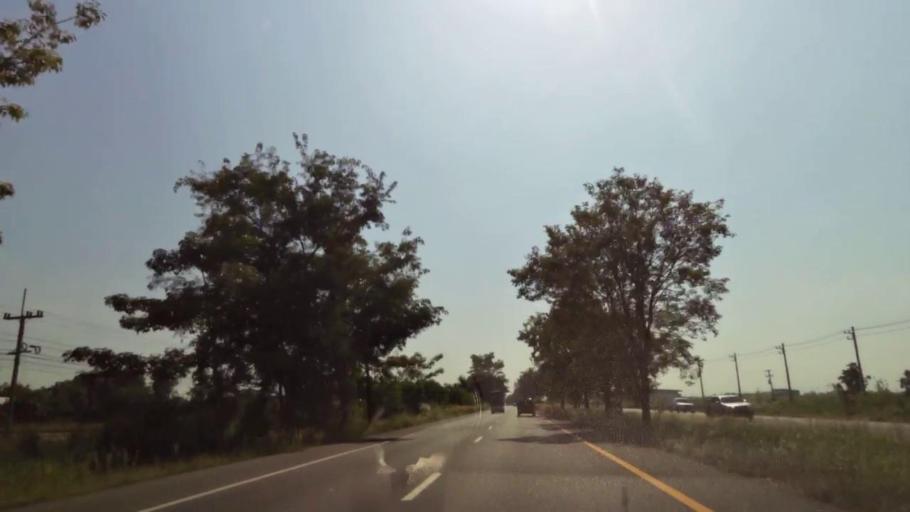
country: TH
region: Nakhon Sawan
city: Kao Liao
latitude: 15.9394
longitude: 100.1136
